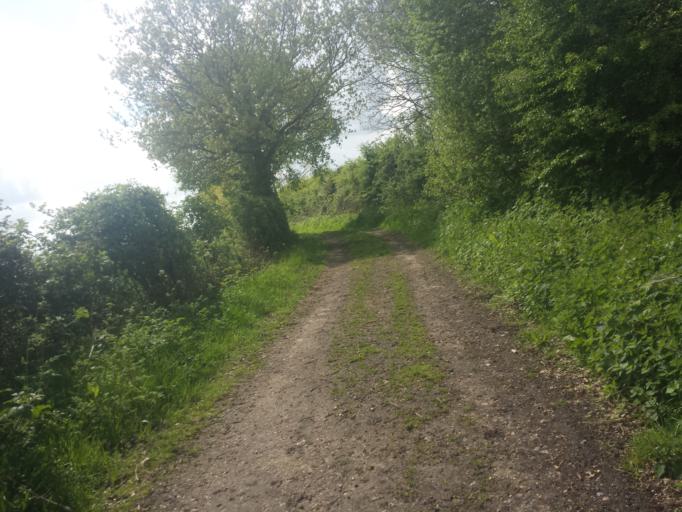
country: GB
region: England
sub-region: Essex
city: Great Bentley
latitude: 51.8806
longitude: 1.0445
